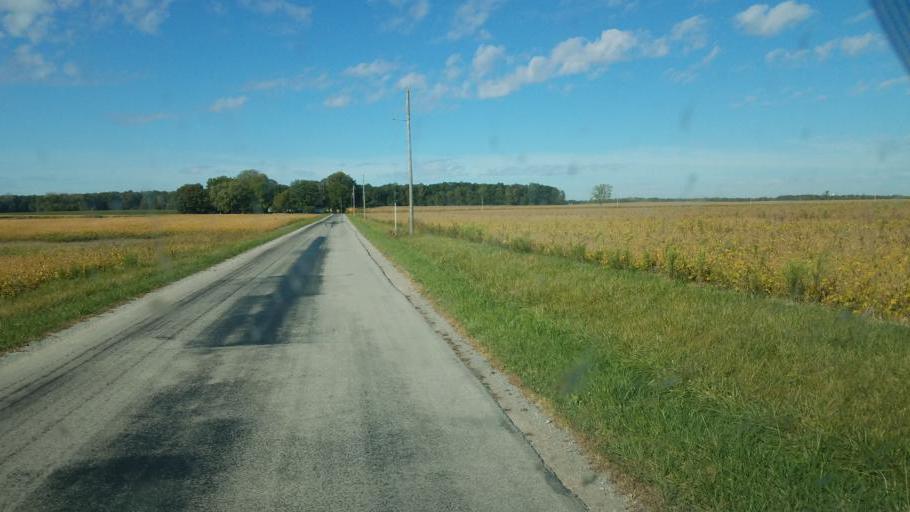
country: US
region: Ohio
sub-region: Wyandot County
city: Upper Sandusky
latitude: 40.8036
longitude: -83.2413
